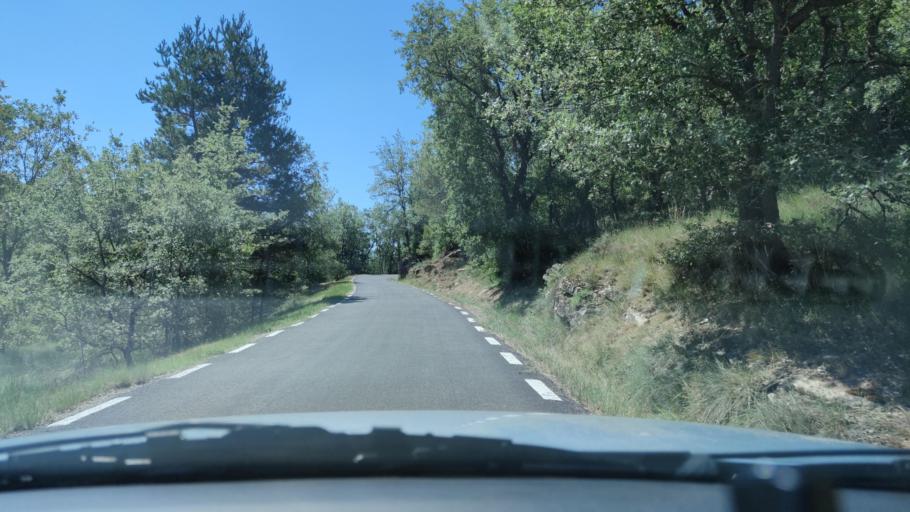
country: ES
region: Catalonia
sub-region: Provincia de Lleida
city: Tora de Riubregos
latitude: 41.8901
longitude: 1.4408
